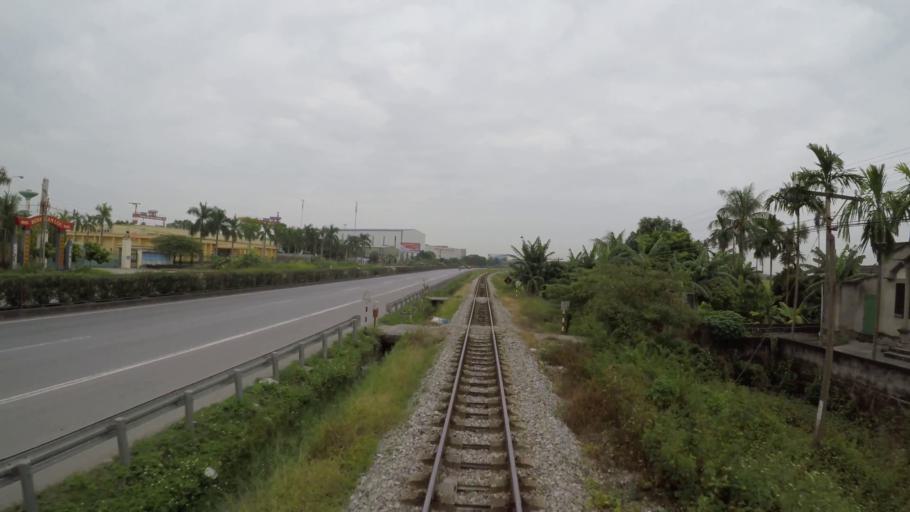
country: VN
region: Hai Duong
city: Phu Thai
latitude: 20.9514
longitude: 106.5323
